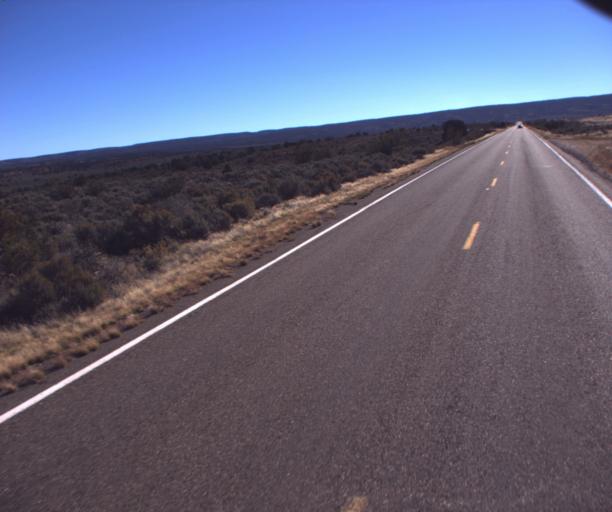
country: US
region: Arizona
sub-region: Coconino County
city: Fredonia
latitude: 36.8686
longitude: -112.3220
